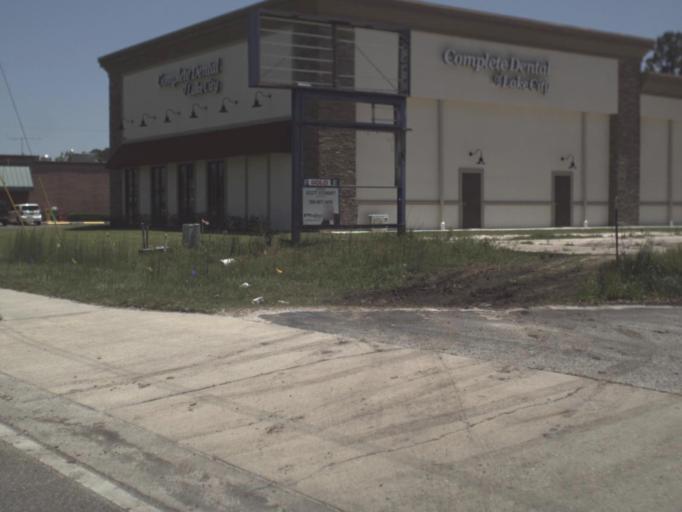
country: US
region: Florida
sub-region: Columbia County
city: Lake City
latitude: 30.1801
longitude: -82.6814
